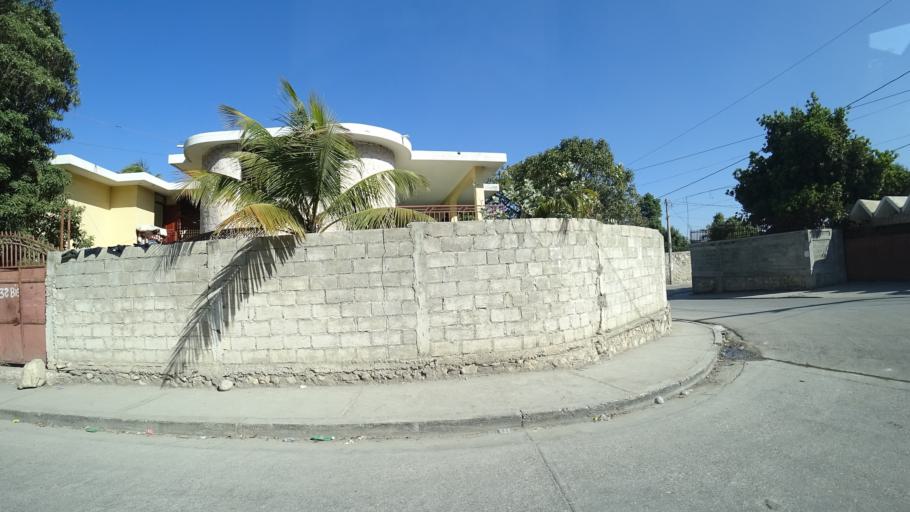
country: HT
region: Ouest
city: Delmas 73
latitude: 18.5577
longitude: -72.3048
